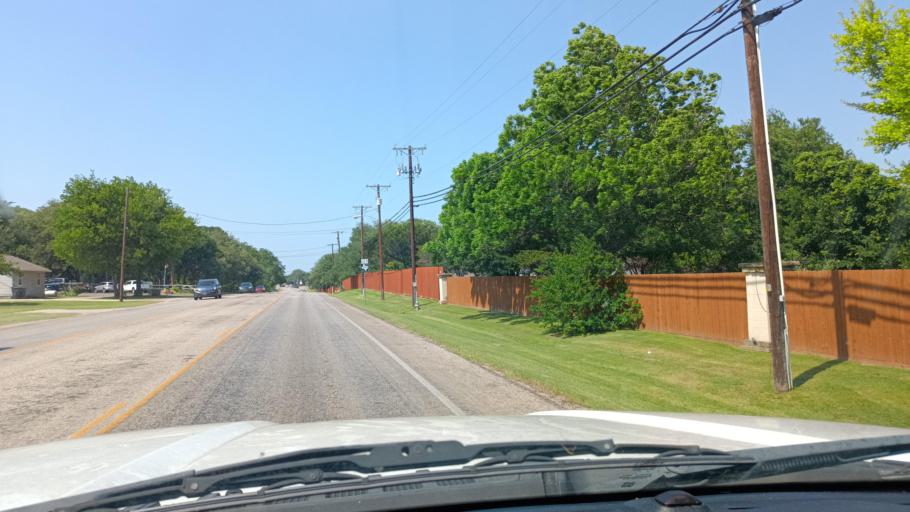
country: US
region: Texas
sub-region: Bell County
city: Morgans Point Resort
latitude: 31.1234
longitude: -97.4705
